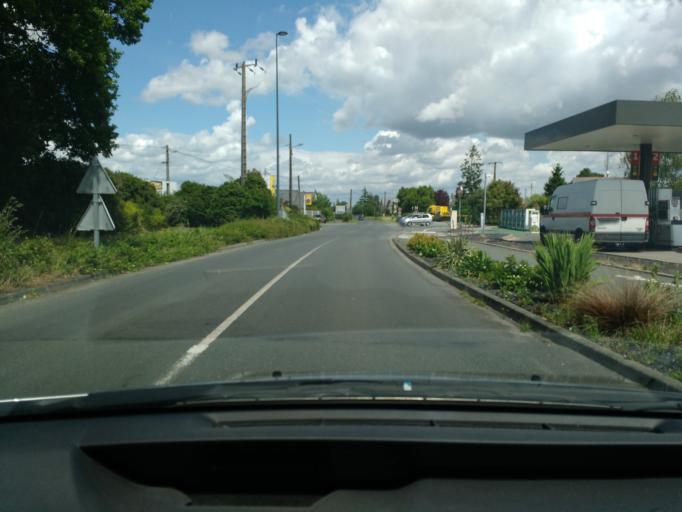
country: FR
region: Pays de la Loire
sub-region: Departement de Maine-et-Loire
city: Trelaze
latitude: 47.4734
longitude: -0.4928
